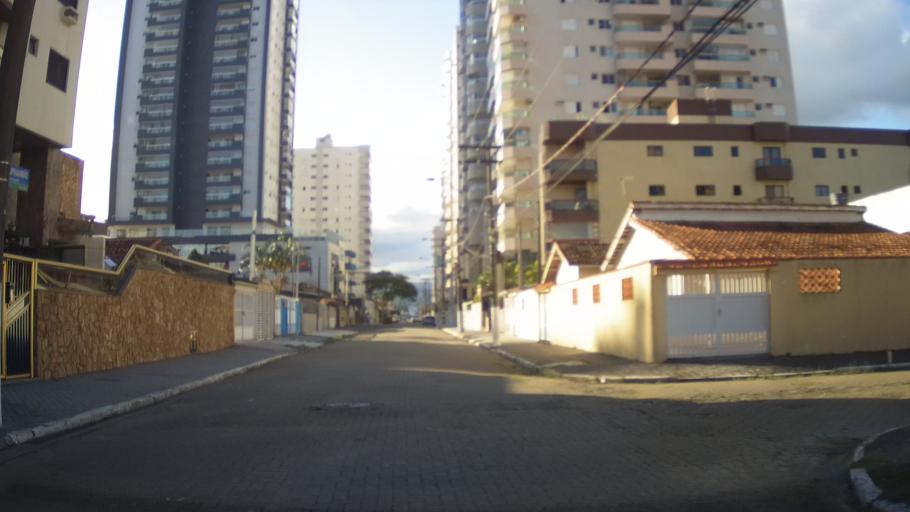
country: BR
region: Sao Paulo
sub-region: Praia Grande
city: Praia Grande
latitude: -24.0208
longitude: -46.4531
